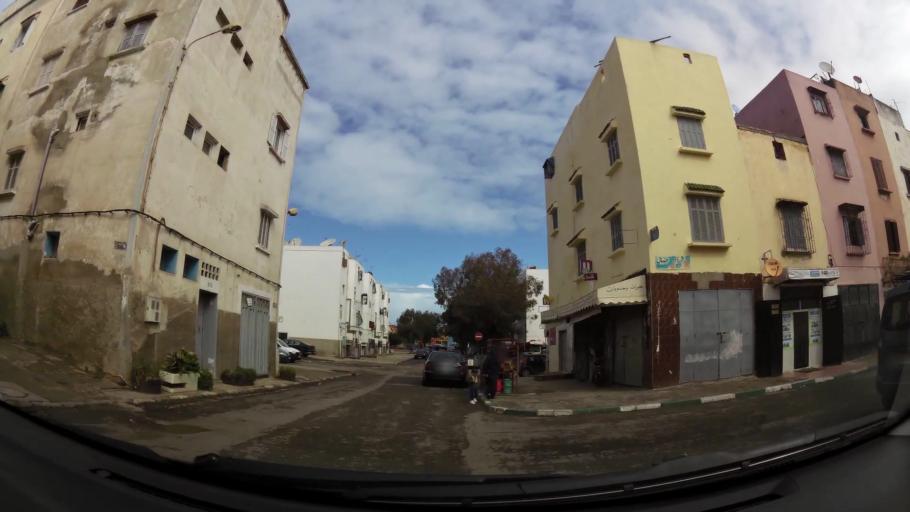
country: MA
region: Grand Casablanca
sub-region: Casablanca
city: Casablanca
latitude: 33.5756
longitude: -7.6736
